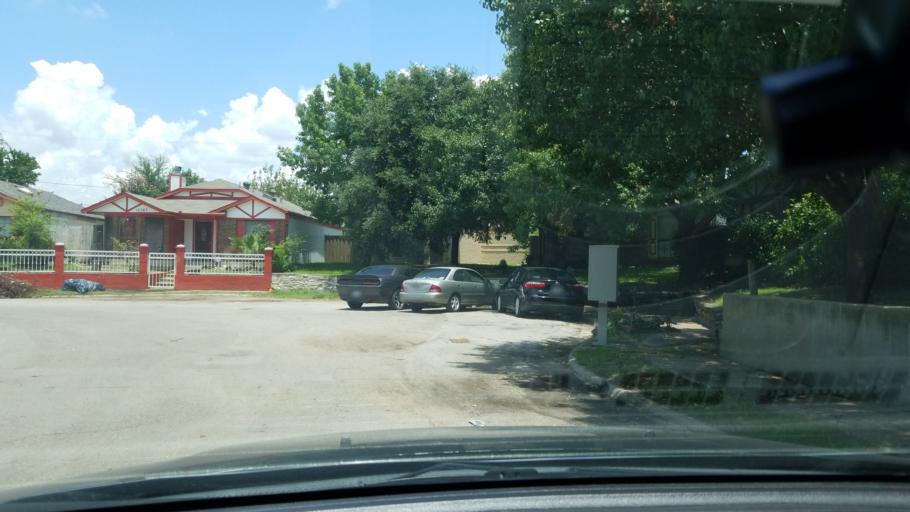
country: US
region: Texas
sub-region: Dallas County
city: Balch Springs
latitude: 32.7437
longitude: -96.6444
